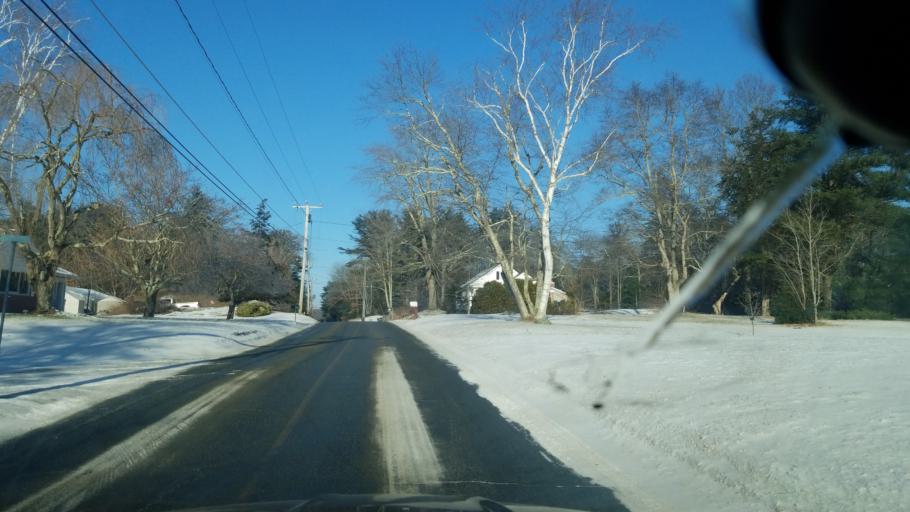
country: US
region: Connecticut
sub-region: Windham County
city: East Brooklyn
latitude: 41.8087
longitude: -71.9052
